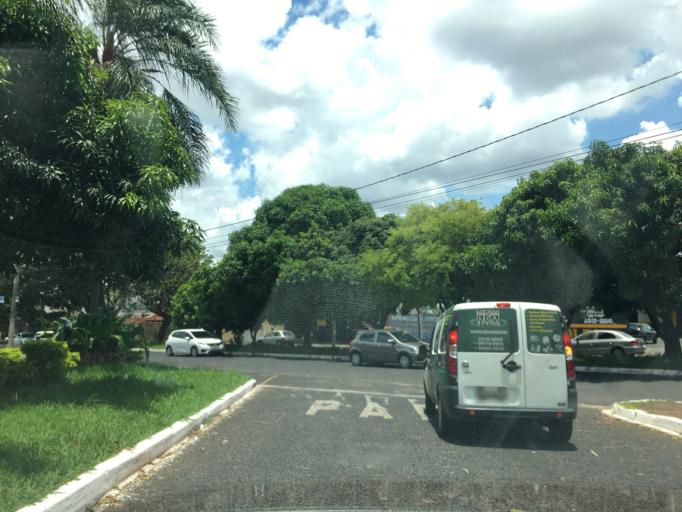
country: BR
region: Minas Gerais
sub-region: Uberlandia
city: Uberlandia
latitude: -18.9323
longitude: -48.3029
